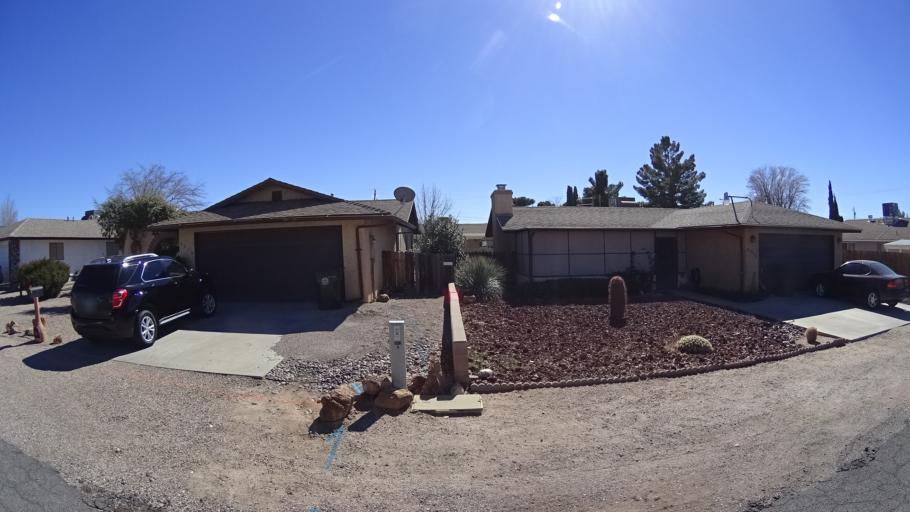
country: US
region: Arizona
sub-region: Mohave County
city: Kingman
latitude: 35.2132
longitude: -114.0309
